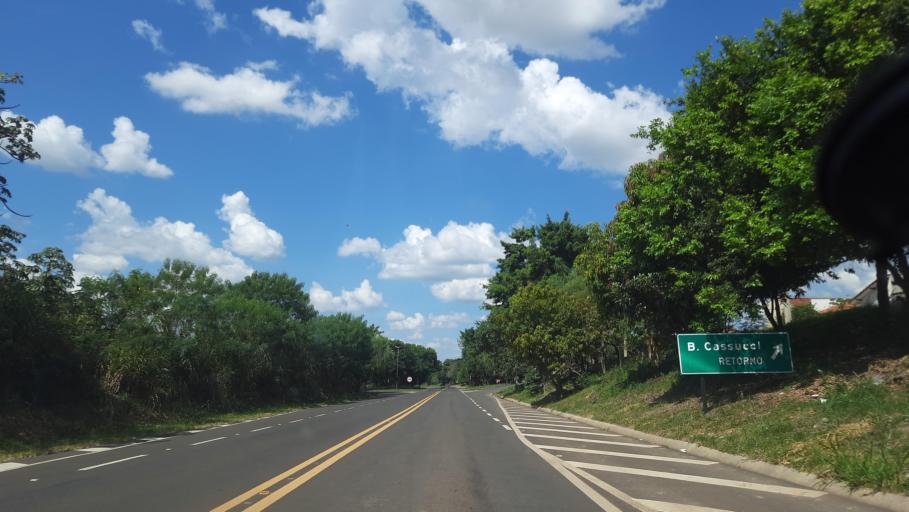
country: BR
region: Sao Paulo
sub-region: Sao Jose Do Rio Pardo
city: Sao Jose do Rio Pardo
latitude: -21.6065
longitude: -46.9334
